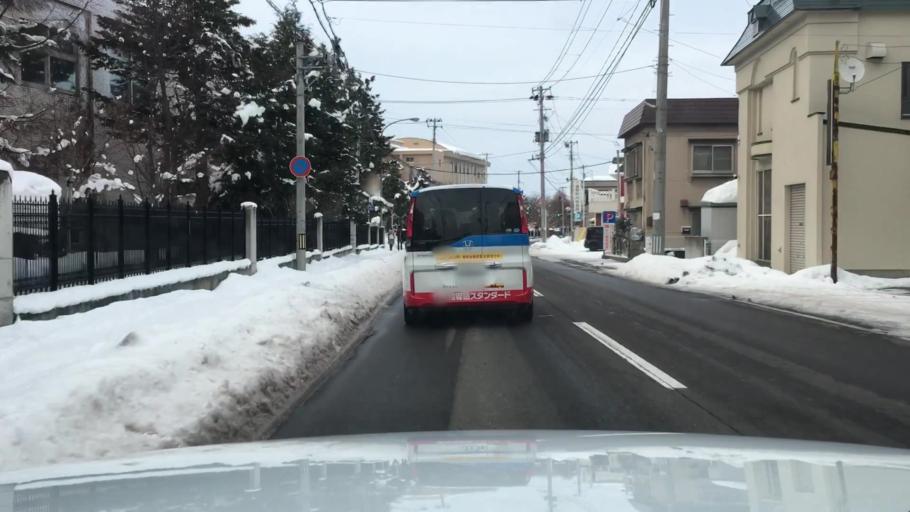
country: JP
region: Aomori
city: Hirosaki
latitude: 40.5879
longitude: 140.4745
